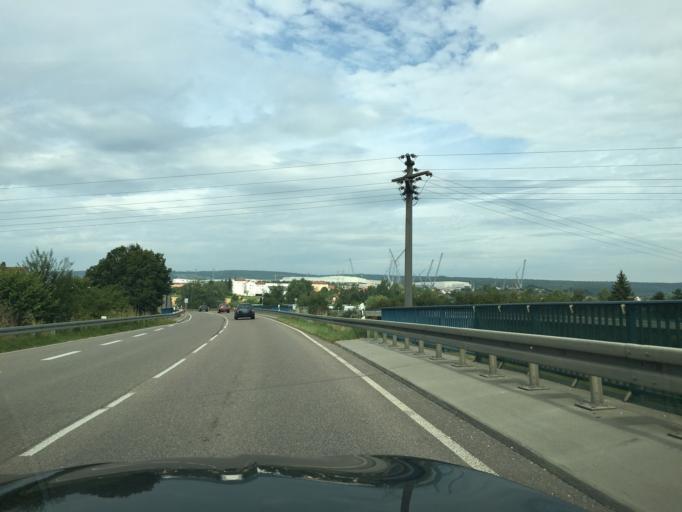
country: DE
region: Baden-Wuerttemberg
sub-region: Tuebingen Region
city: Ehingen
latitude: 48.2900
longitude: 9.7318
